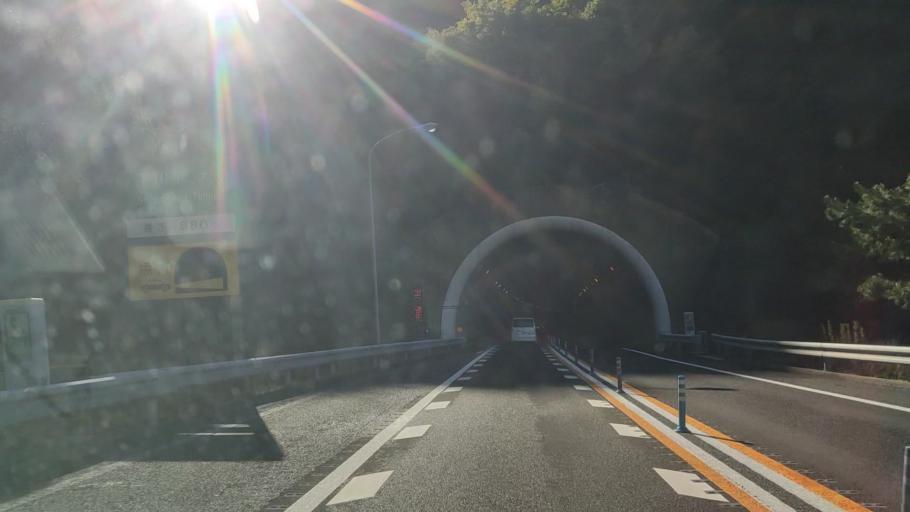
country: JP
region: Ehime
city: Kawanoecho
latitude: 33.9989
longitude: 133.6412
